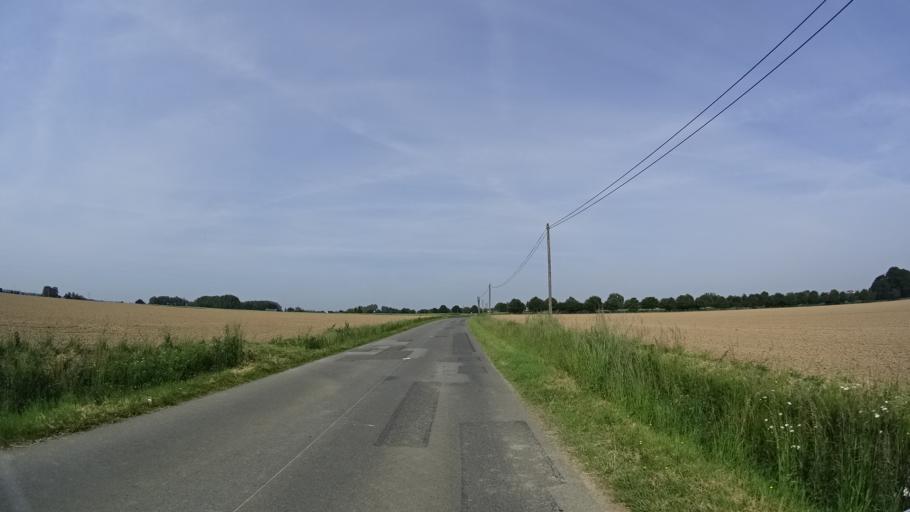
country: FR
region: Brittany
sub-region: Departement d'Ille-et-Vilaine
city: Chateaugiron
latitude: 48.0332
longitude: -1.5060
